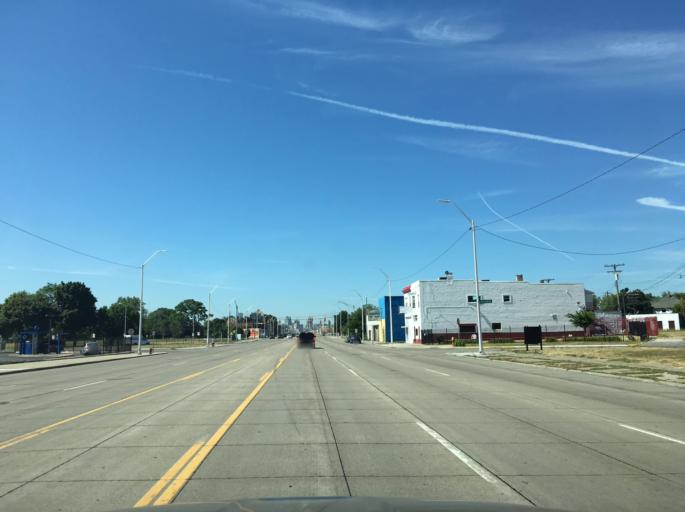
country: US
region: Michigan
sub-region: Wayne County
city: Hamtramck
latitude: 42.3756
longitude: -83.0168
